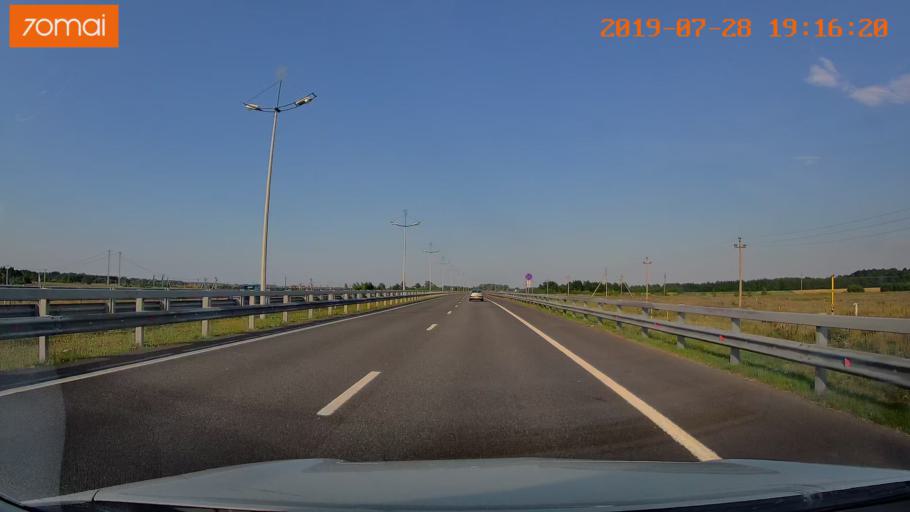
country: RU
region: Kaliningrad
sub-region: Zelenogradskiy Rayon
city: Zelenogradsk
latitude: 54.9214
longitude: 20.3735
